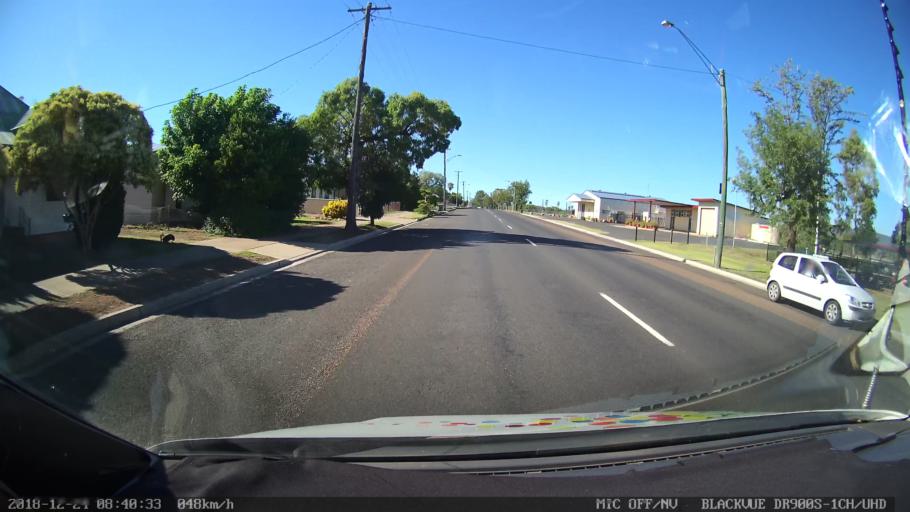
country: AU
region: New South Wales
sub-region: Liverpool Plains
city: Quirindi
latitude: -31.3557
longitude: 150.6464
